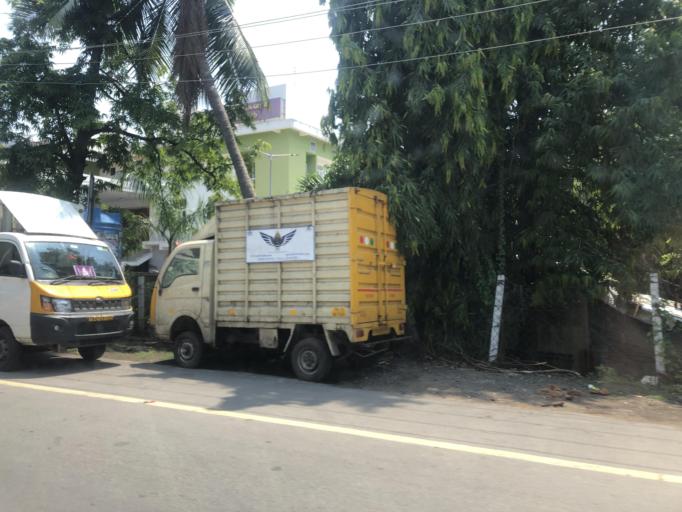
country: IN
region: Tamil Nadu
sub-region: Chennai
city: Gandhi Nagar
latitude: 12.9849
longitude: 80.2595
